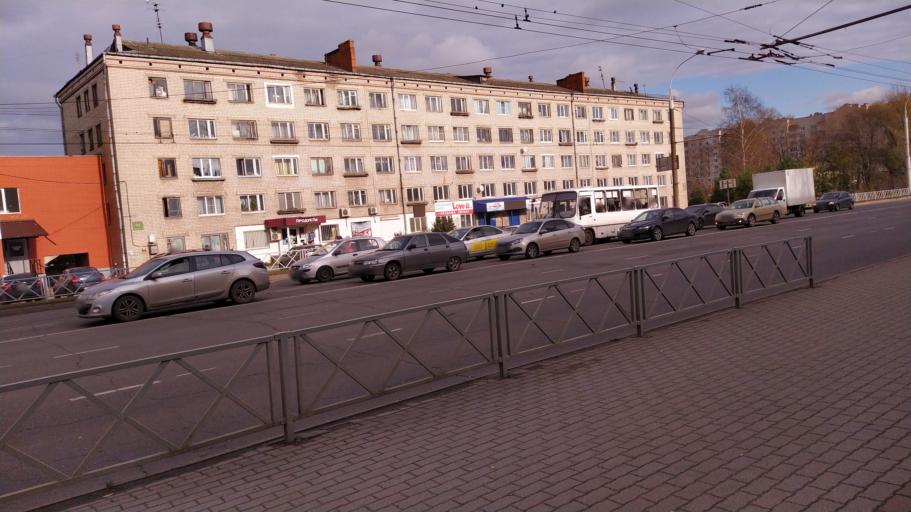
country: RU
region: Jaroslavl
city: Rybinsk
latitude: 58.0562
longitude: 38.7983
